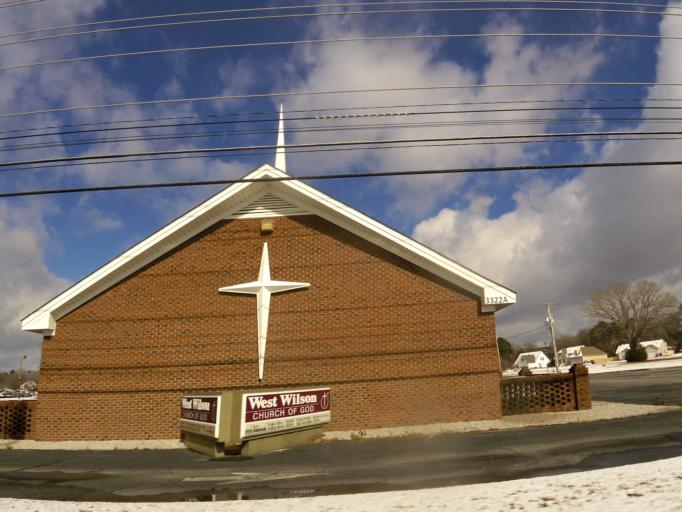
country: US
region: North Carolina
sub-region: Wilson County
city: Wilson
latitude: 35.7211
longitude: -77.9662
